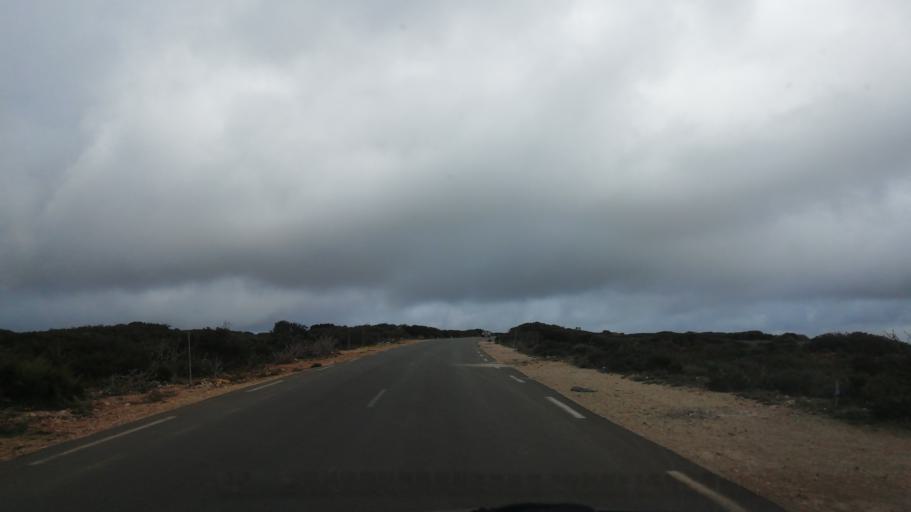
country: DZ
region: Oran
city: Mers el Kebir
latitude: 35.7038
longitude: -0.7384
